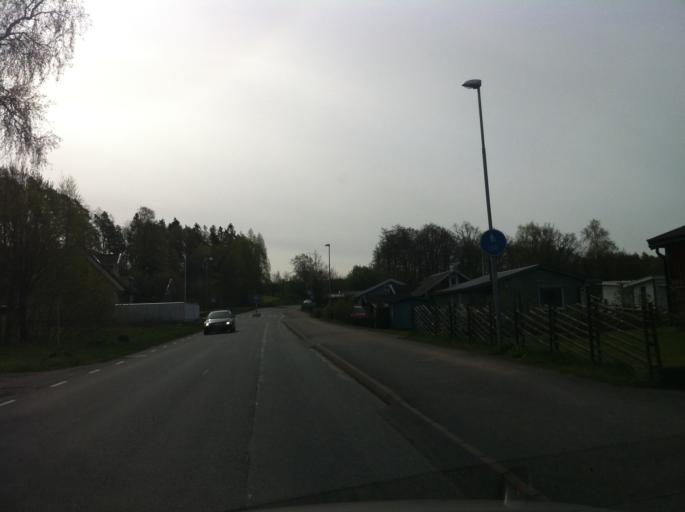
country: SE
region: Vaestra Goetaland
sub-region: Marks Kommun
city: Kinna
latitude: 57.4703
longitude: 12.7120
